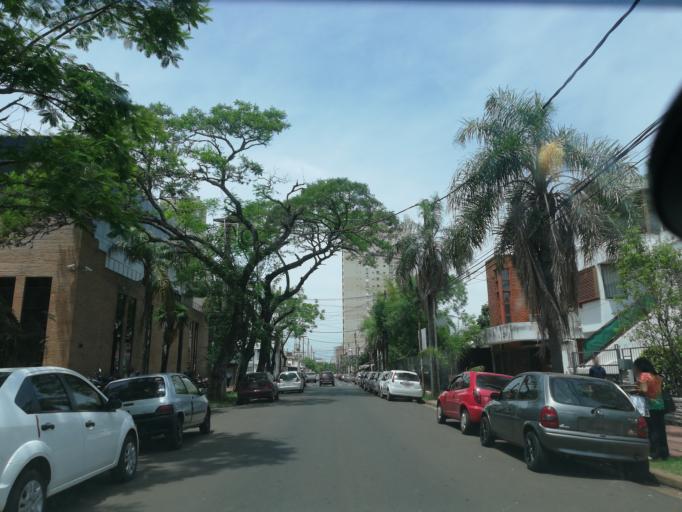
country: AR
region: Misiones
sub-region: Departamento de Capital
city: Posadas
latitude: -27.3555
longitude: -55.8941
